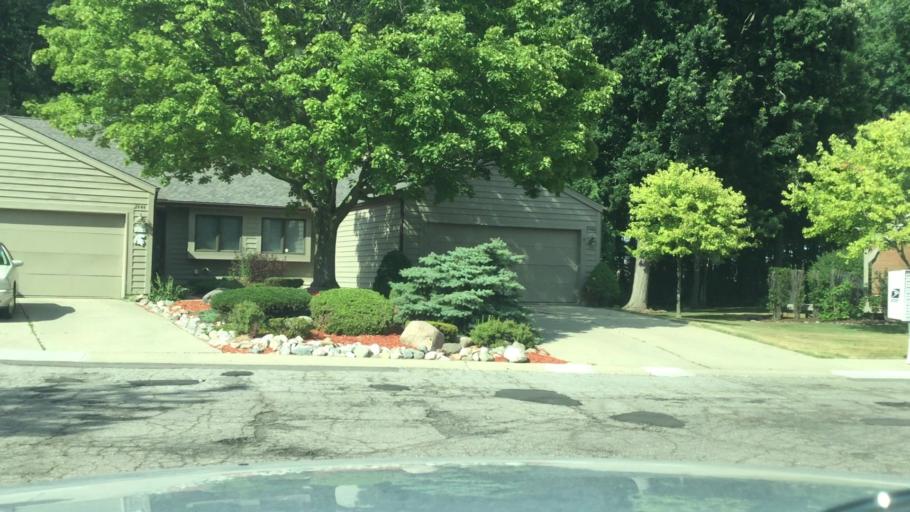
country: US
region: Michigan
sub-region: Genesee County
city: Swartz Creek
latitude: 42.9955
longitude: -83.7766
